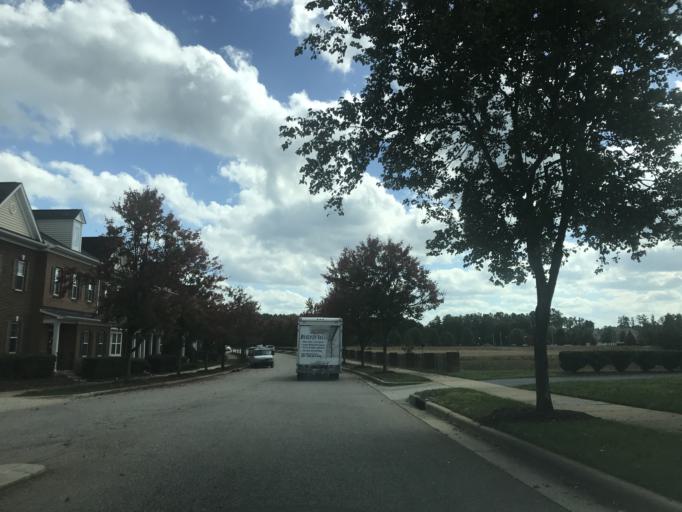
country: US
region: North Carolina
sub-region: Wake County
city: Raleigh
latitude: 35.7356
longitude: -78.6583
